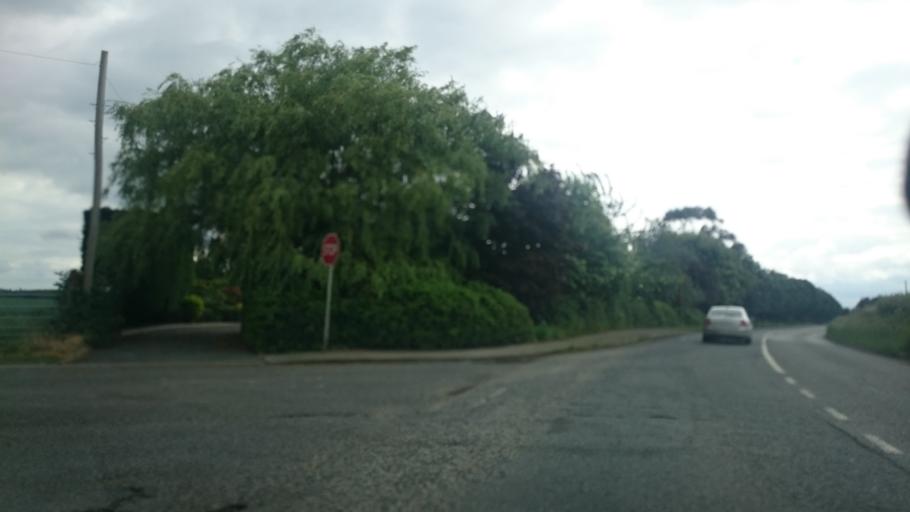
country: IE
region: Leinster
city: Lusk
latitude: 53.5052
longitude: -6.1870
